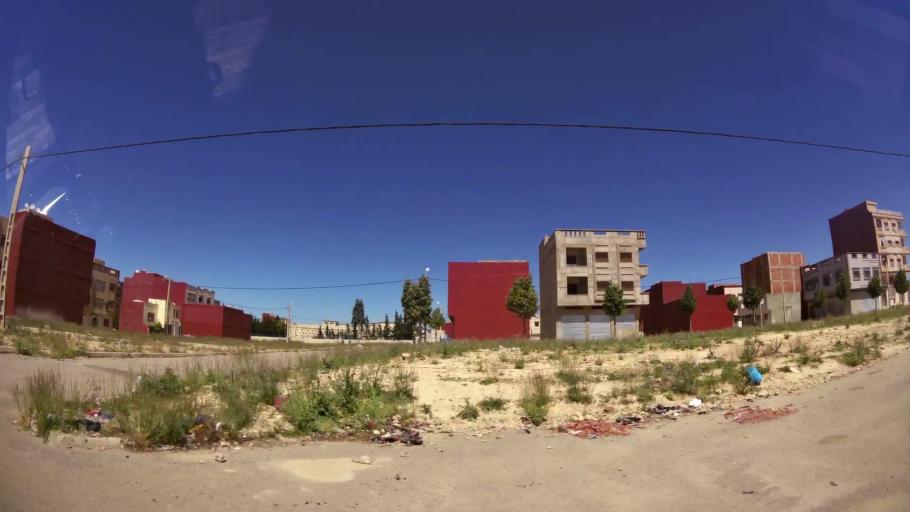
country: MA
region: Oriental
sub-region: Oujda-Angad
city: Oujda
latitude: 34.6574
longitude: -1.8711
